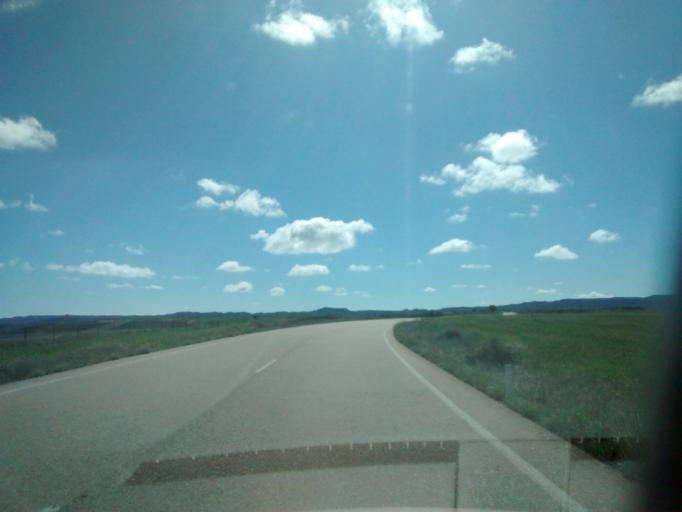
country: ES
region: Aragon
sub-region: Provincia de Zaragoza
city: Lecinena
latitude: 41.7957
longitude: -0.6466
